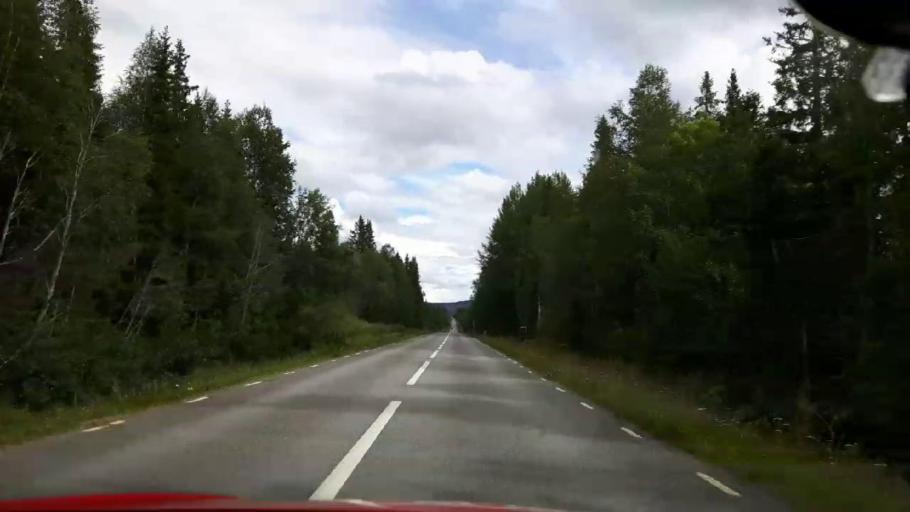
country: NO
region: Nord-Trondelag
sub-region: Lierne
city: Sandvika
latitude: 64.3898
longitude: 14.4225
